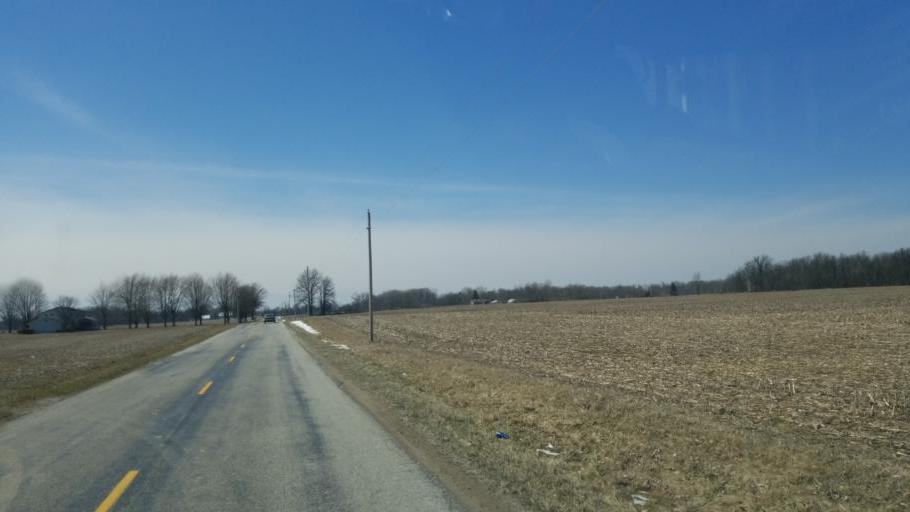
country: US
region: Ohio
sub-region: Crawford County
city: Bucyrus
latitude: 40.6750
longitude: -82.9295
